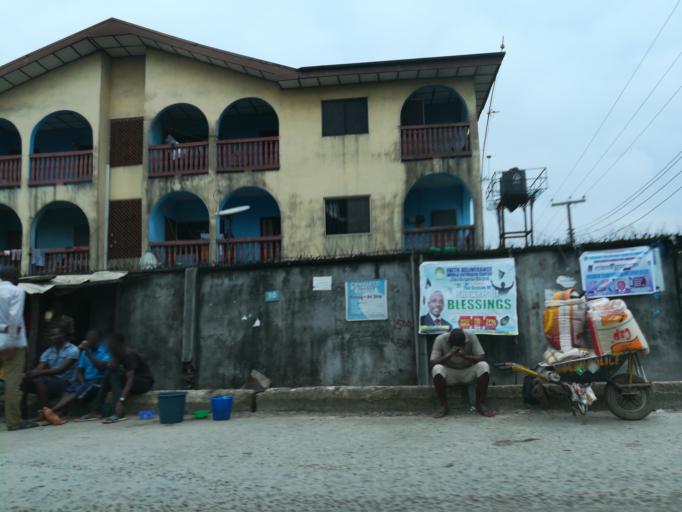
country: NG
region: Rivers
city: Port Harcourt
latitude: 4.7597
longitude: 7.0113
